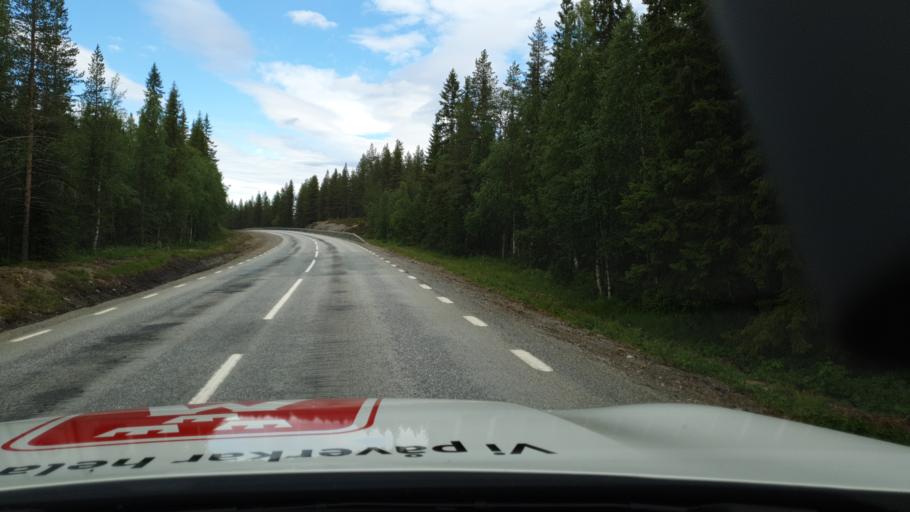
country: SE
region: Vaesterbotten
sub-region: Storumans Kommun
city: Fristad
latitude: 65.3511
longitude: 16.5917
